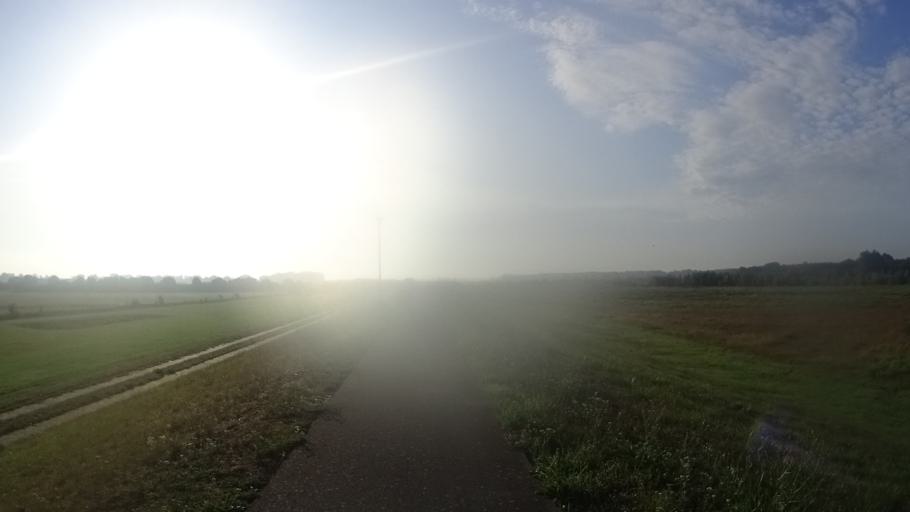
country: DE
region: Brandenburg
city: Lenzen
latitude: 53.0608
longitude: 11.5175
